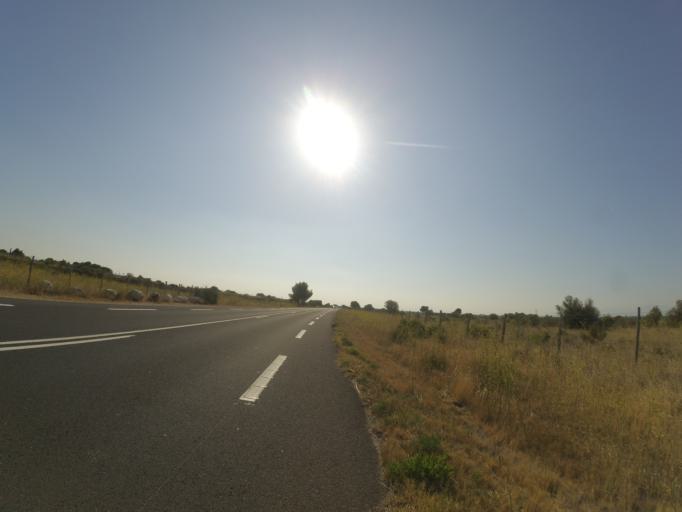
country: FR
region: Languedoc-Roussillon
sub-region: Departement des Pyrenees-Orientales
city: Rivesaltes
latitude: 42.7976
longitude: 2.8653
